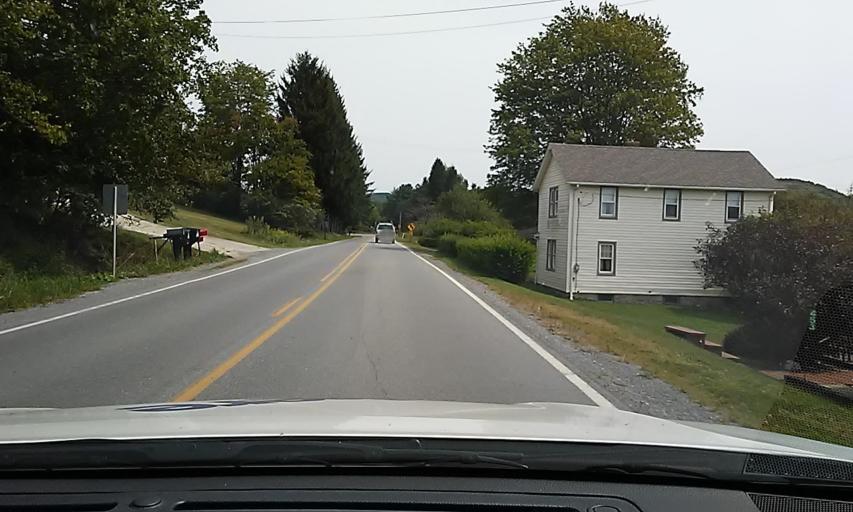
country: US
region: Pennsylvania
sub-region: Elk County
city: Ridgway
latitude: 41.3165
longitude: -78.6443
